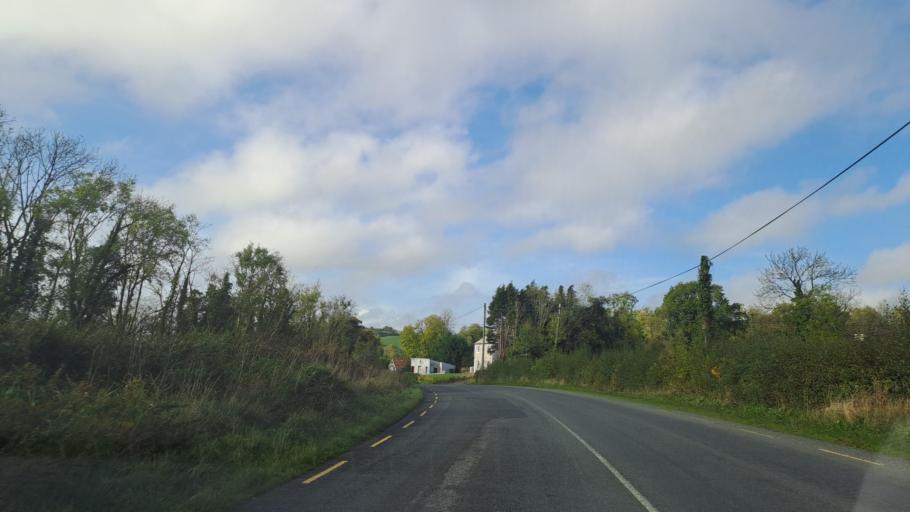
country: IE
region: Ulster
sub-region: An Cabhan
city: Cootehill
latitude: 54.0442
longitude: -6.9892
